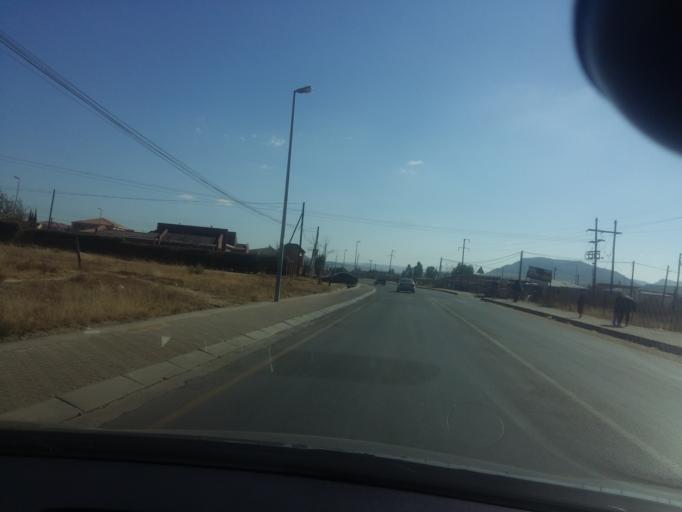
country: LS
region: Maseru
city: Maseru
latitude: -29.3417
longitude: 27.4507
